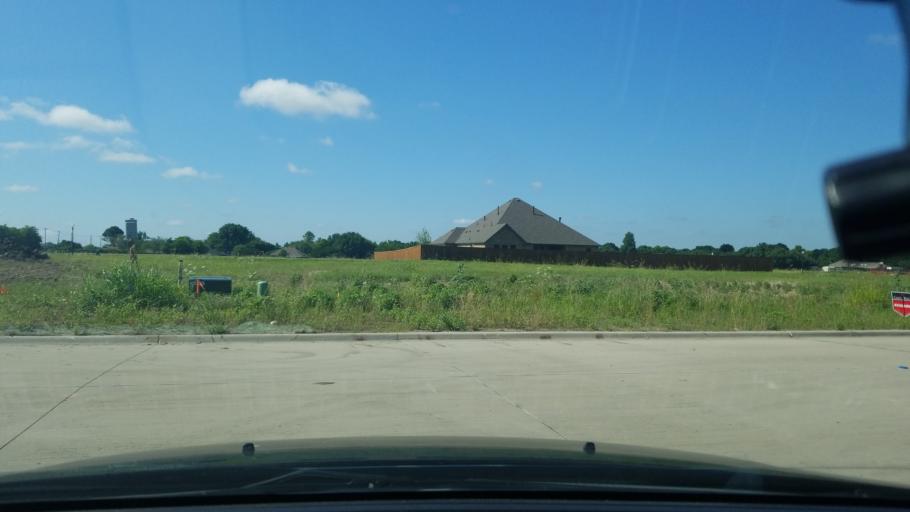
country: US
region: Texas
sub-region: Dallas County
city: Sunnyvale
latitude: 32.8042
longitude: -96.5803
